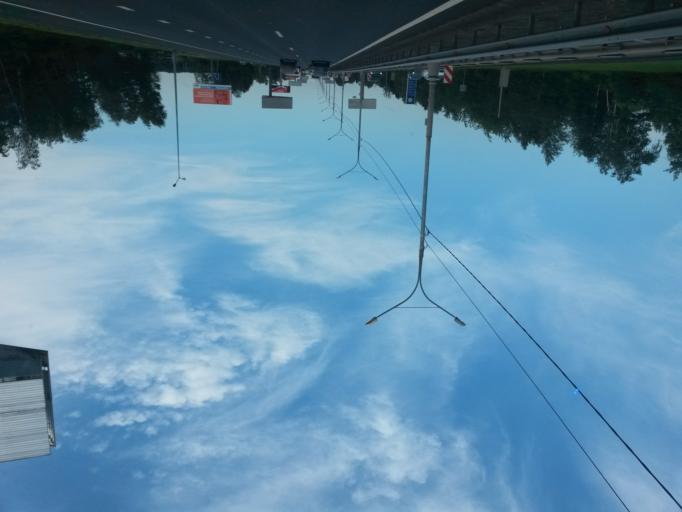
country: RU
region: Moskovskaya
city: Petrovskaya
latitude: 55.5315
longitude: 37.8132
